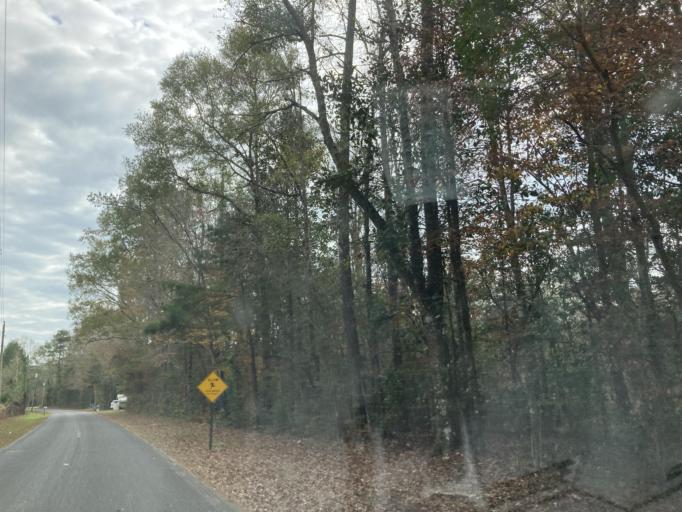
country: US
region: Mississippi
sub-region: Perry County
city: New Augusta
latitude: 31.0718
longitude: -89.1658
